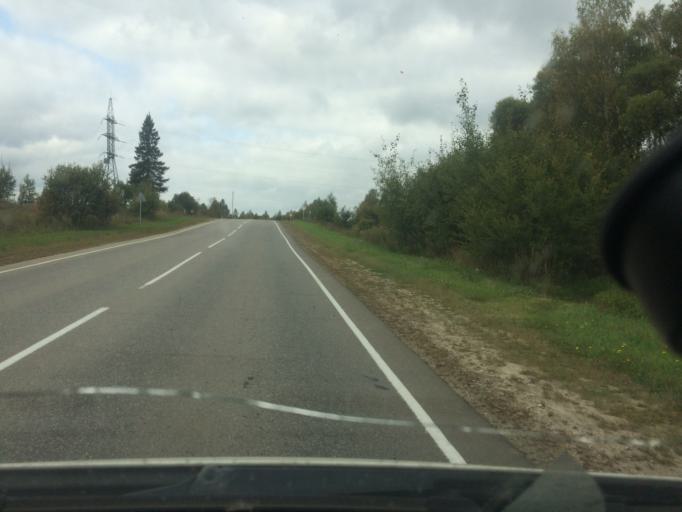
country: RU
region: Tula
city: Suvorov
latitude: 54.0393
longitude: 36.5911
